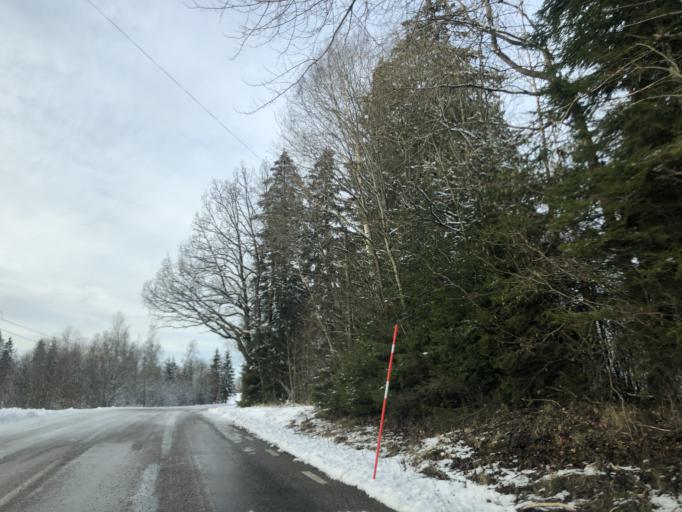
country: SE
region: Vaestra Goetaland
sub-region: Ulricehamns Kommun
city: Ulricehamn
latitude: 57.8106
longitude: 13.5389
